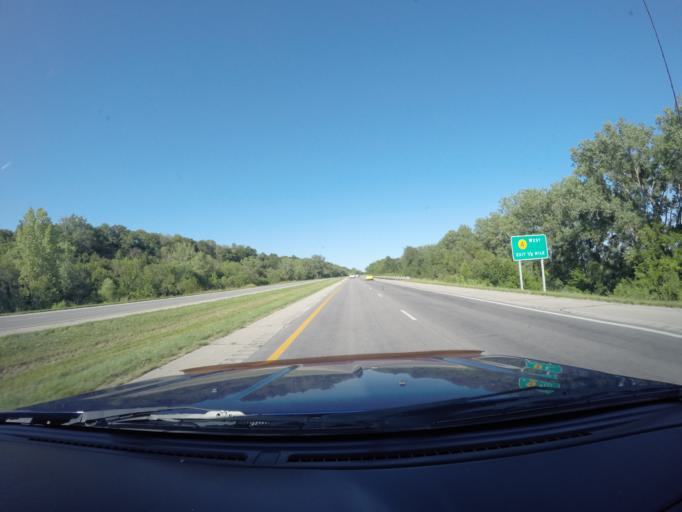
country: US
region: Kansas
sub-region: Shawnee County
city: Topeka
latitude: 39.0921
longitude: -95.6220
